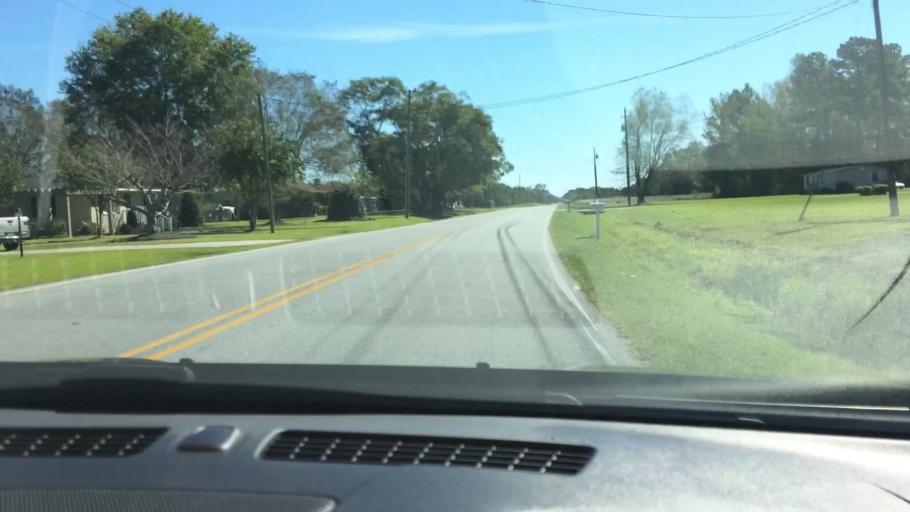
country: US
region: North Carolina
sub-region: Pitt County
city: Grifton
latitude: 35.3960
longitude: -77.3969
